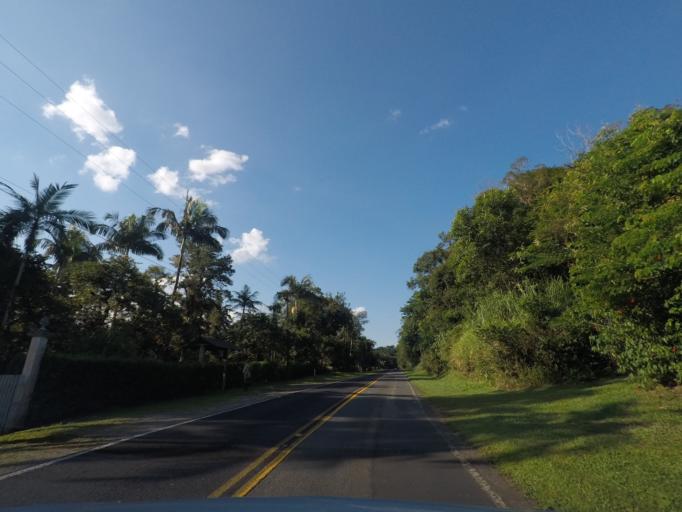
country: BR
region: Parana
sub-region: Antonina
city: Antonina
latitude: -25.3989
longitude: -48.8718
